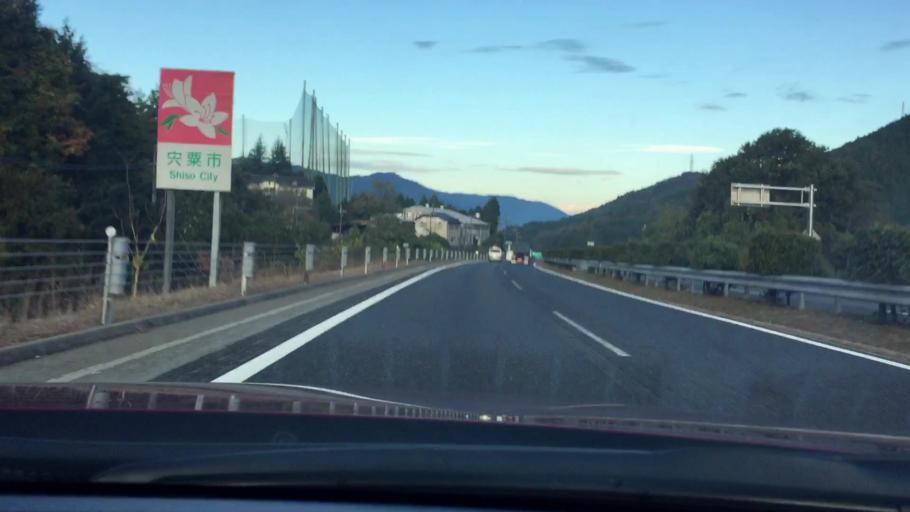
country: JP
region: Hyogo
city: Yamazakicho-nakabirose
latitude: 34.9919
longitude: 134.5761
